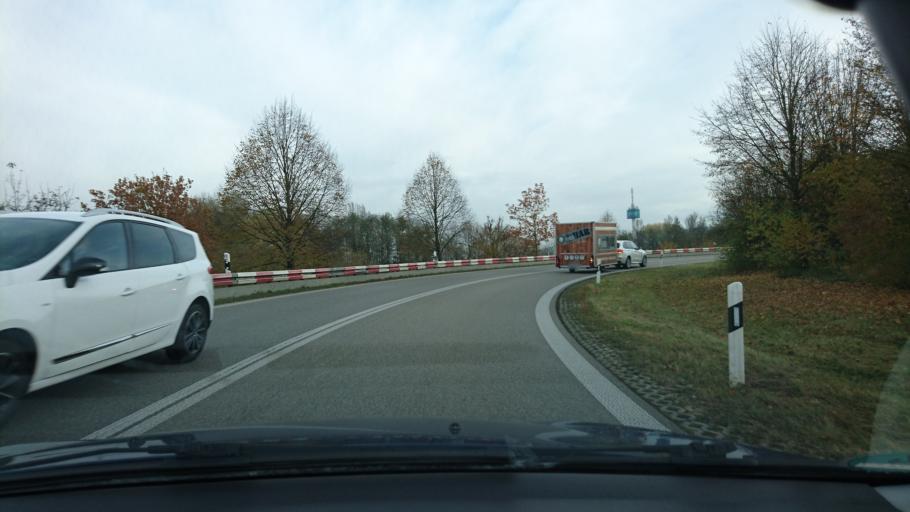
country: DE
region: Baden-Wuerttemberg
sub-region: Regierungsbezirk Stuttgart
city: Schorndorf
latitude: 48.8092
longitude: 9.5042
